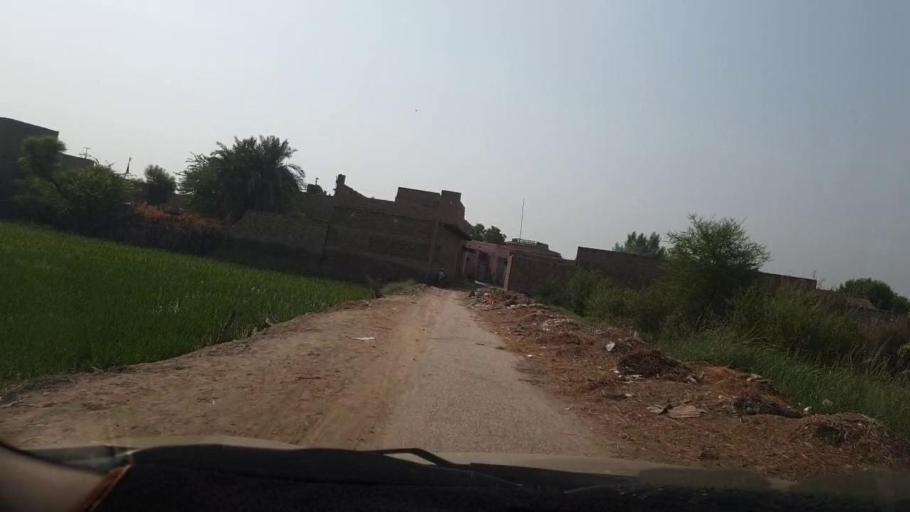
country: PK
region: Sindh
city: Goth Garelo
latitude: 27.4343
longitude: 68.0437
